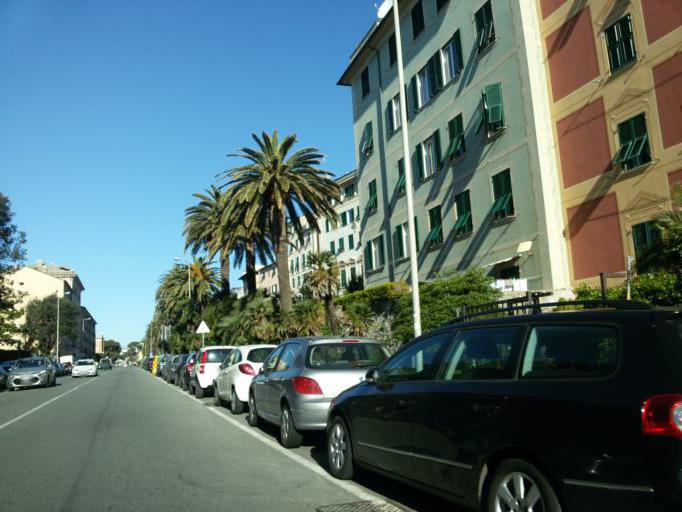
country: IT
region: Liguria
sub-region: Provincia di Genova
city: Bogliasco
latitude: 44.3835
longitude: 9.0236
